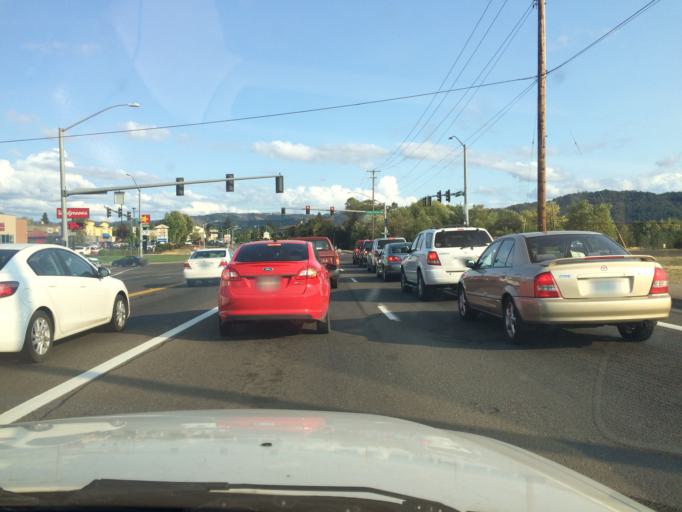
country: US
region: Oregon
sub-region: Douglas County
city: Roseburg
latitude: 43.2323
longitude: -123.3738
